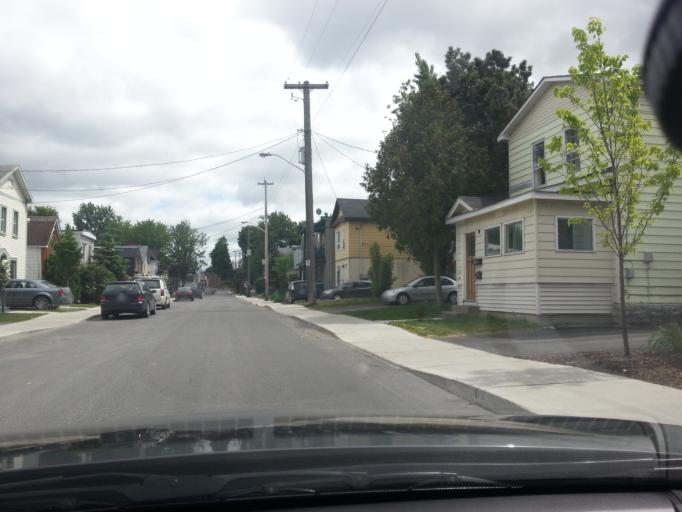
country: CA
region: Ontario
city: Ottawa
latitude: 45.4060
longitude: -75.7271
